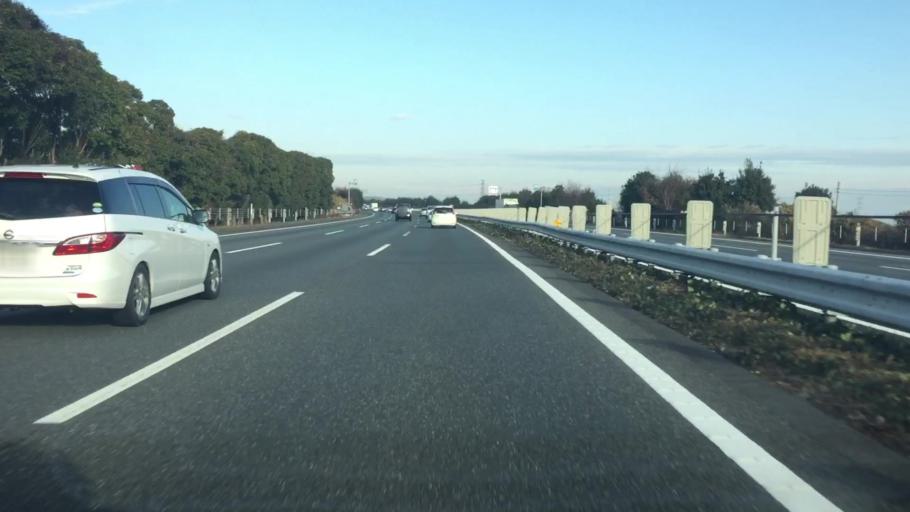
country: JP
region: Saitama
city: Honjo
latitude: 36.1903
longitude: 139.1897
